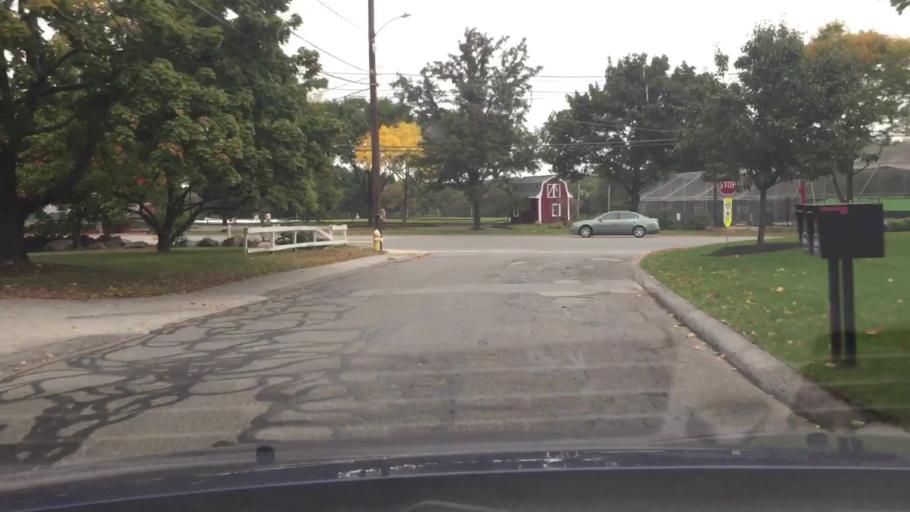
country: US
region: Massachusetts
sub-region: Essex County
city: Middleton
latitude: 42.5818
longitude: -71.0043
